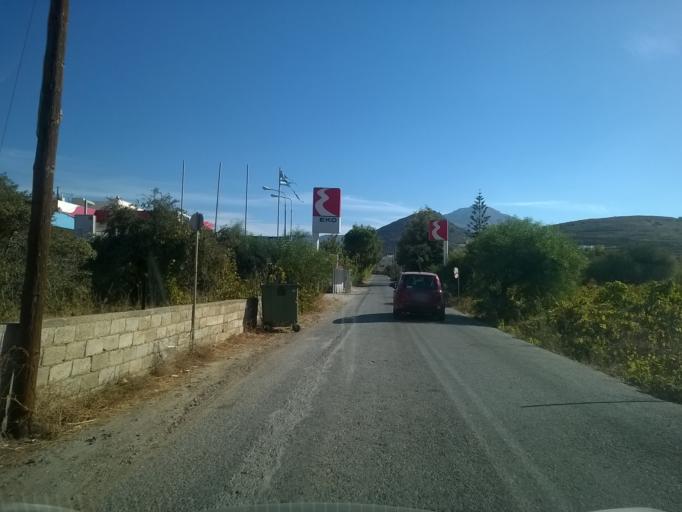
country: GR
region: South Aegean
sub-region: Nomos Kykladon
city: Naxos
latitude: 37.1151
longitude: 25.4295
